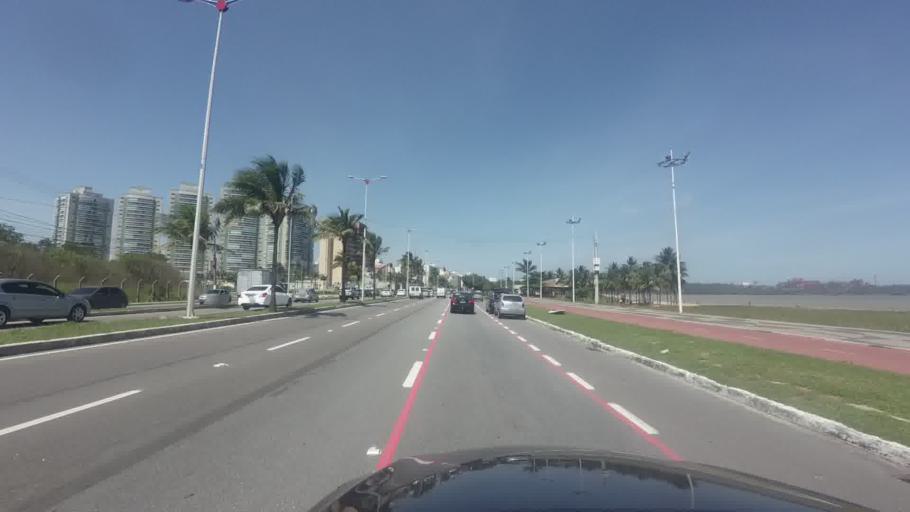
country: BR
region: Espirito Santo
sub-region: Vila Velha
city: Vila Velha
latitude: -20.2679
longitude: -40.2717
